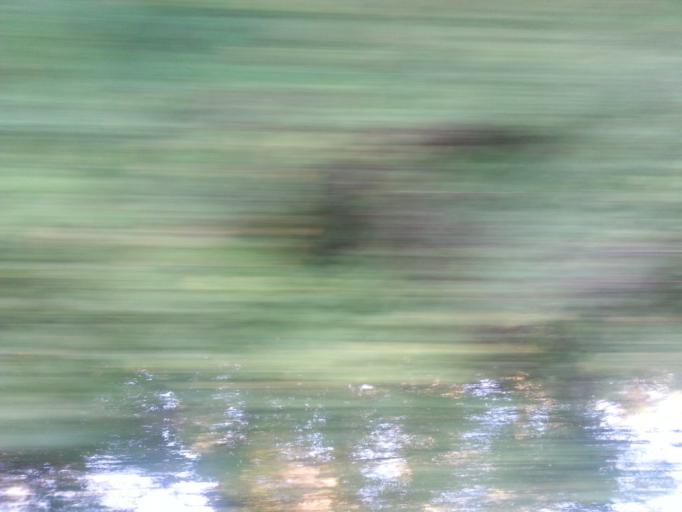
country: US
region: Tennessee
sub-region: Blount County
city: Wildwood
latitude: 35.8671
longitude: -83.8929
